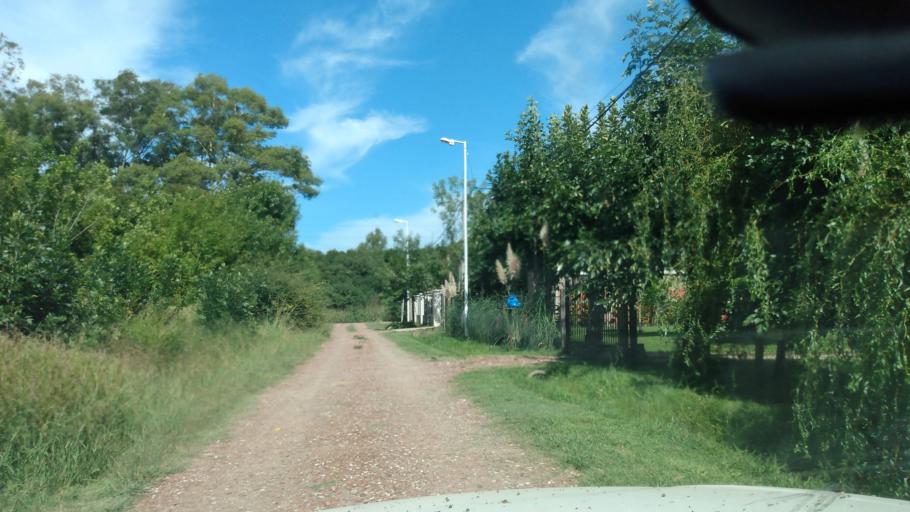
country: AR
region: Buenos Aires
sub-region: Partido de Lujan
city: Lujan
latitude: -34.5517
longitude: -59.1505
